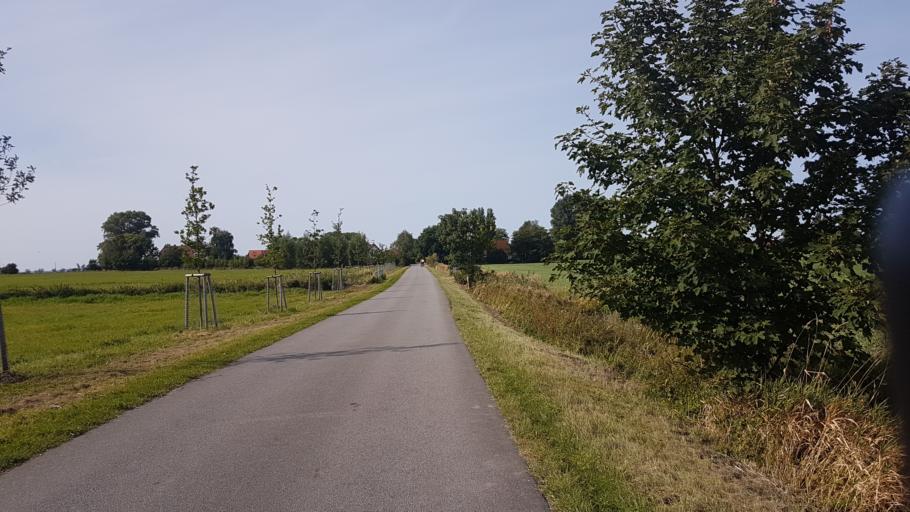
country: DE
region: Mecklenburg-Vorpommern
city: Gingst
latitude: 54.4226
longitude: 13.2291
